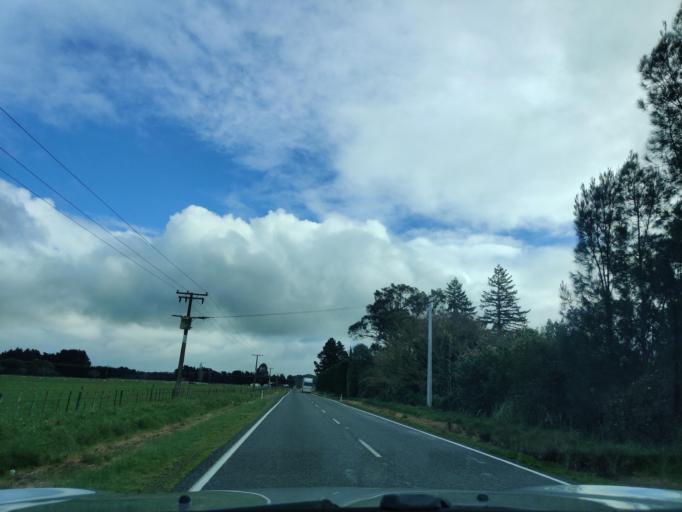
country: NZ
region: Hawke's Bay
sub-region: Hastings District
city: Hastings
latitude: -40.0203
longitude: 176.3390
